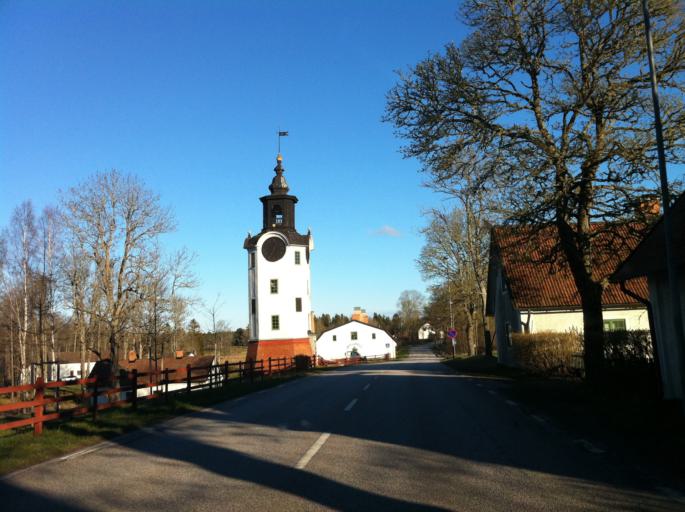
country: SE
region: Uppsala
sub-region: Osthammars Kommun
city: Anneberg
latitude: 60.1844
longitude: 18.3961
